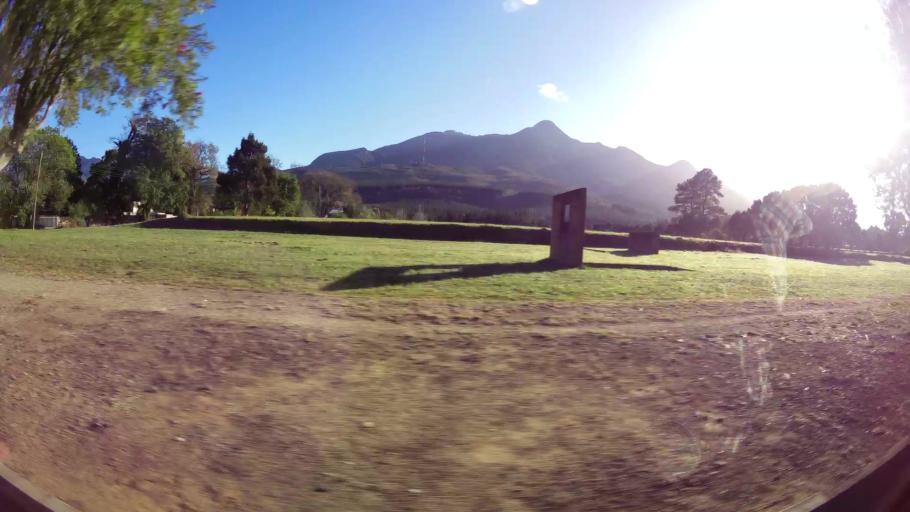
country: ZA
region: Western Cape
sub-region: Eden District Municipality
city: George
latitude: -33.9470
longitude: 22.4501
